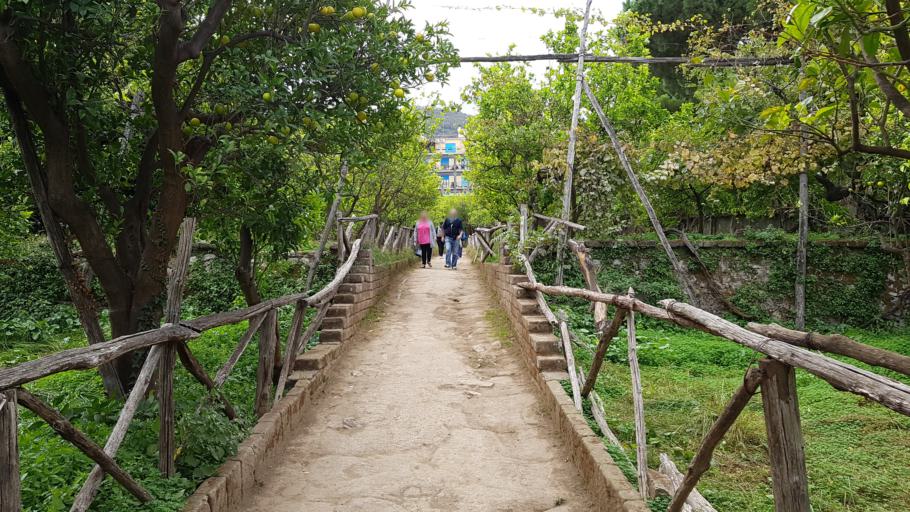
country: IT
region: Campania
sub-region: Provincia di Napoli
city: Sorrento
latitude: 40.6279
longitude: 14.3807
